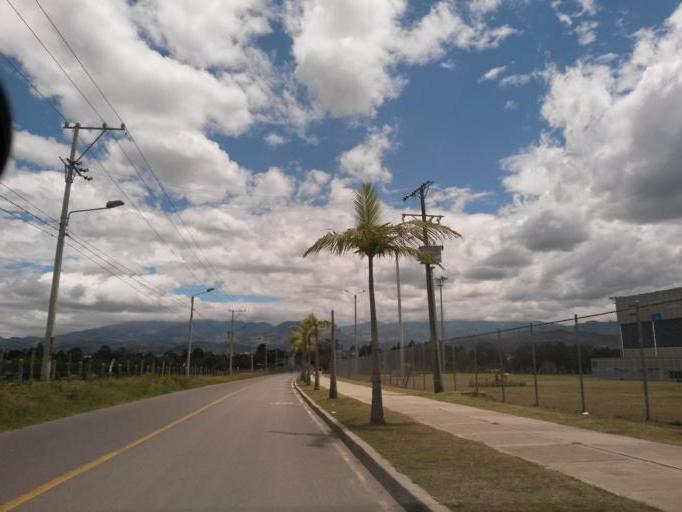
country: CO
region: Cauca
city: Popayan
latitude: 2.4904
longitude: -76.5922
